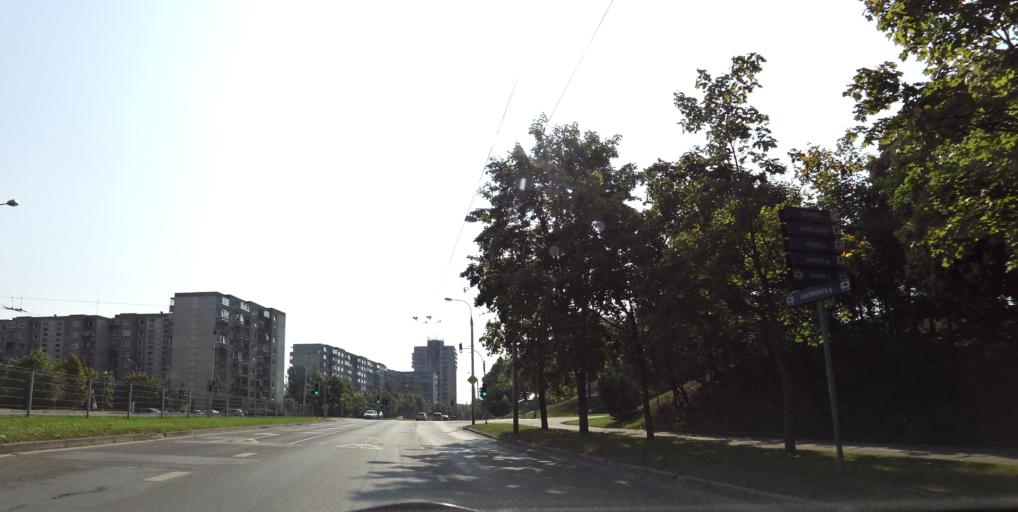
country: LT
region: Vilnius County
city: Justiniskes
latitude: 54.7218
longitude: 25.2223
